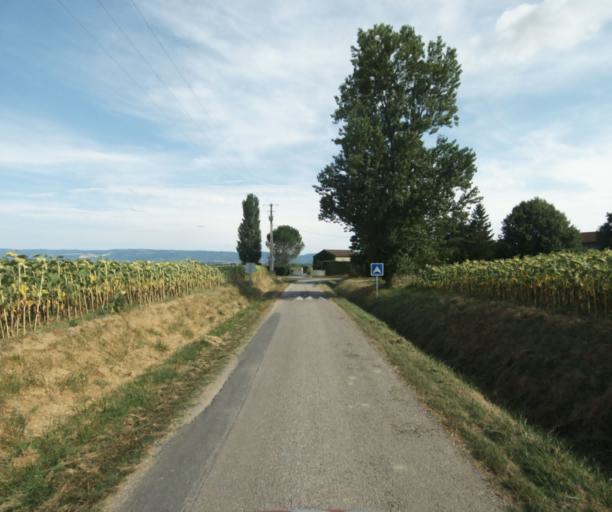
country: FR
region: Midi-Pyrenees
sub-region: Departement du Tarn
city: Puylaurens
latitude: 43.5316
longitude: 1.9914
